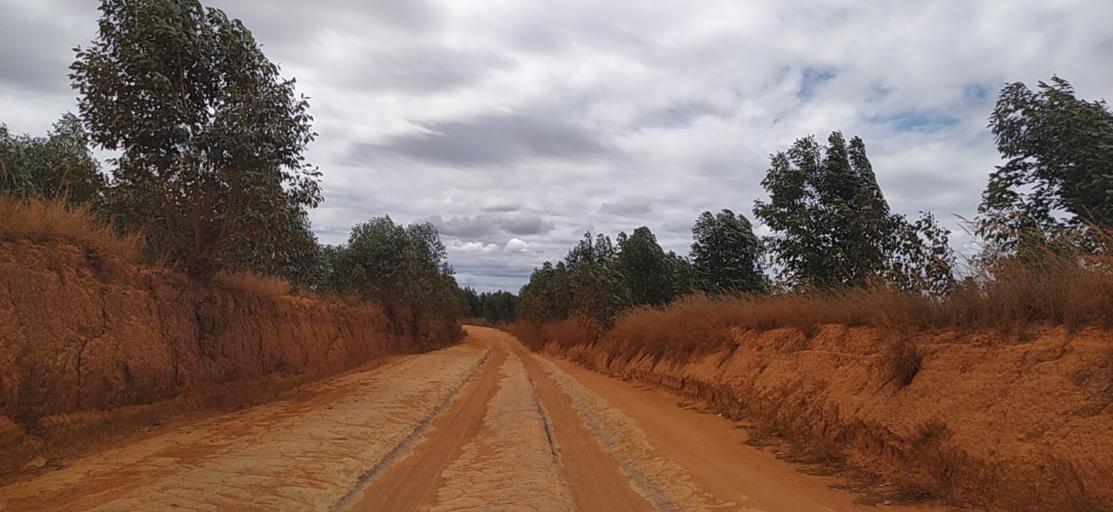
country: MG
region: Alaotra Mangoro
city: Ambatondrazaka
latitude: -18.0447
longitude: 48.2494
